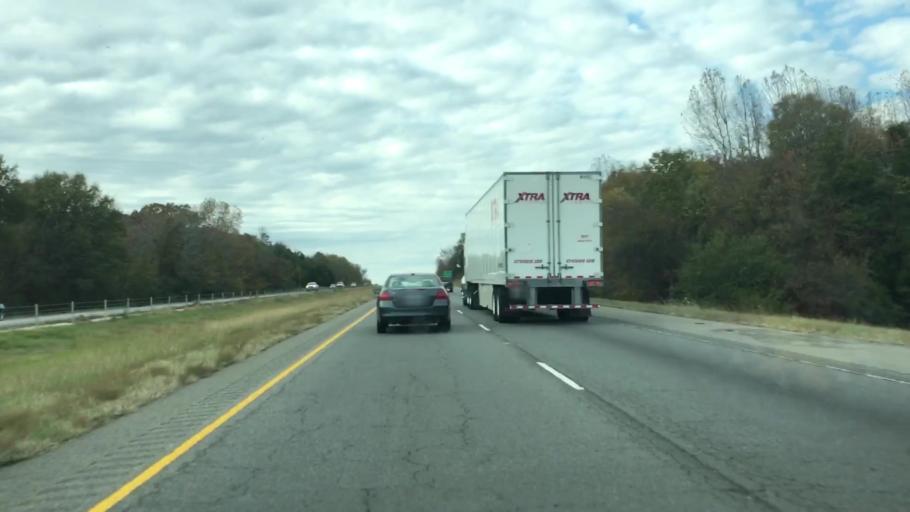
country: US
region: Arkansas
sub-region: Faulkner County
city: Conway
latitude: 35.1428
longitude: -92.5307
